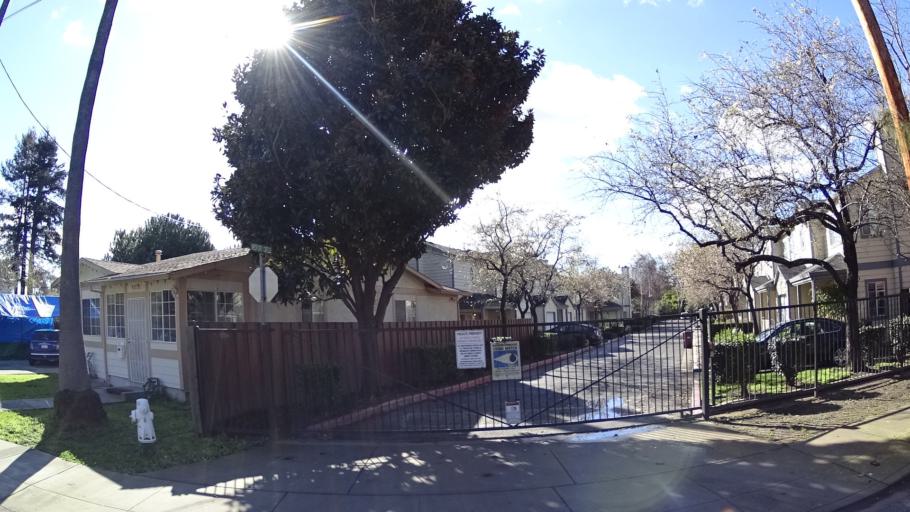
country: US
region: California
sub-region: Alameda County
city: Cherryland
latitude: 37.6829
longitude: -122.1068
